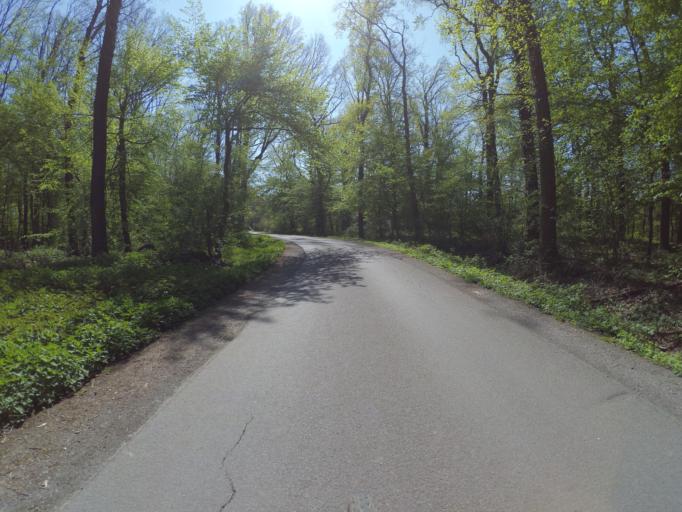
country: DE
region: North Rhine-Westphalia
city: Ludinghausen
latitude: 51.7602
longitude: 7.4387
